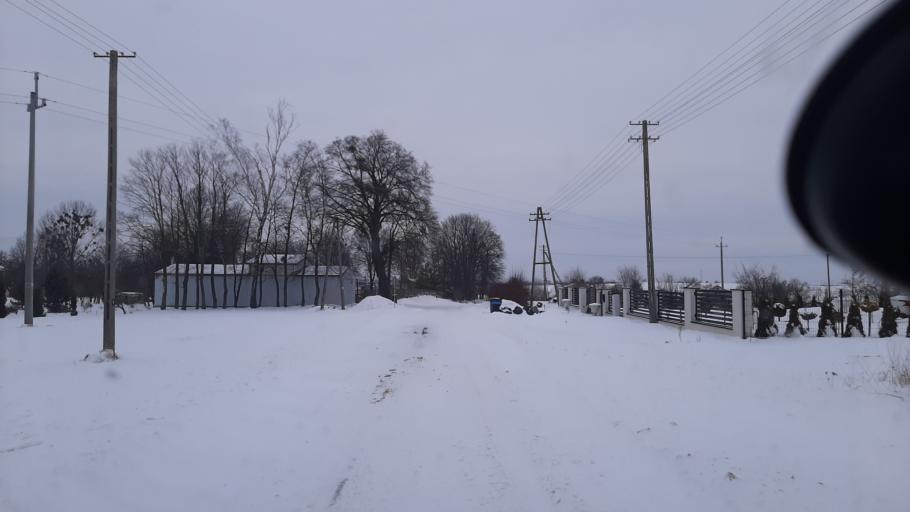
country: PL
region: Lublin Voivodeship
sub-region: Powiat lubelski
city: Garbow
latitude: 51.3325
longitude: 22.2912
